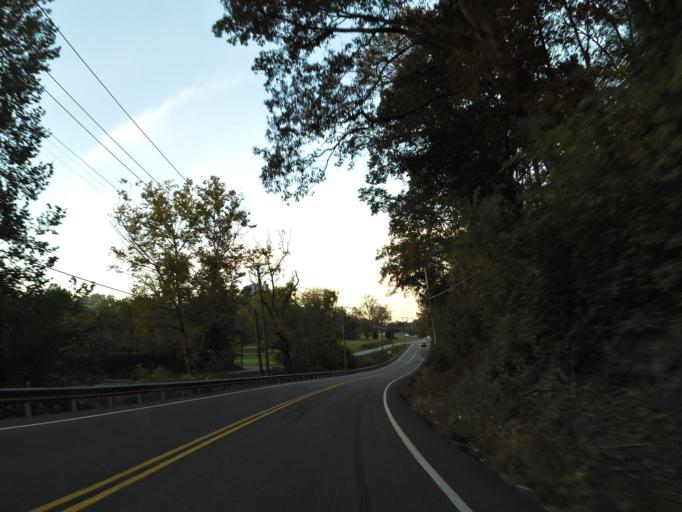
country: US
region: Tennessee
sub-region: Knox County
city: Knoxville
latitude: 35.8925
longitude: -83.9373
